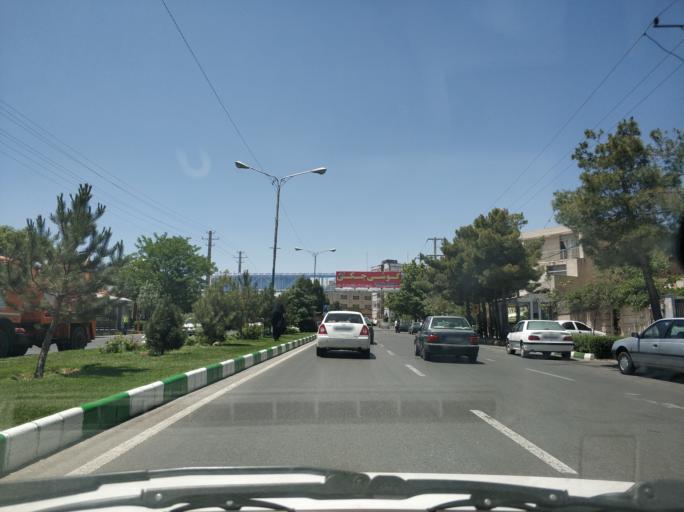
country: IR
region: Razavi Khorasan
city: Mashhad
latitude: 36.3133
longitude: 59.4916
